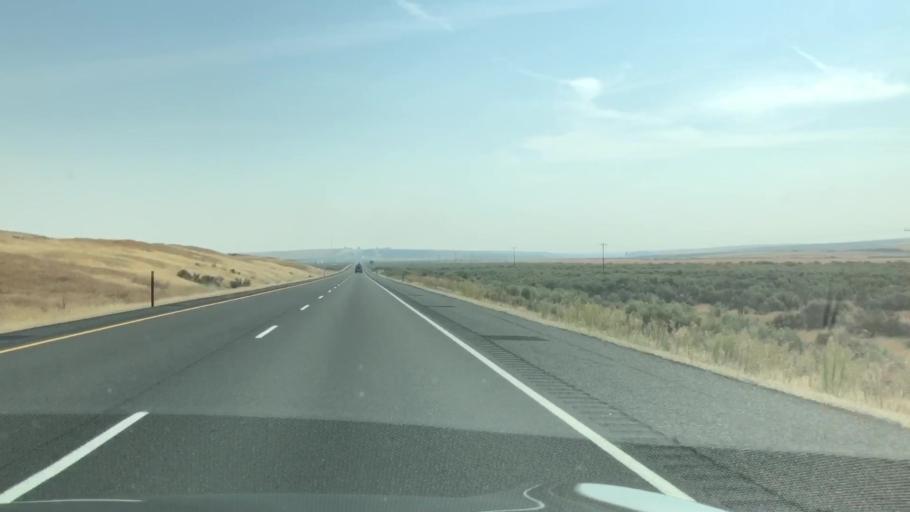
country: US
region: Washington
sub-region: Grant County
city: Warden
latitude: 47.0871
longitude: -118.9129
